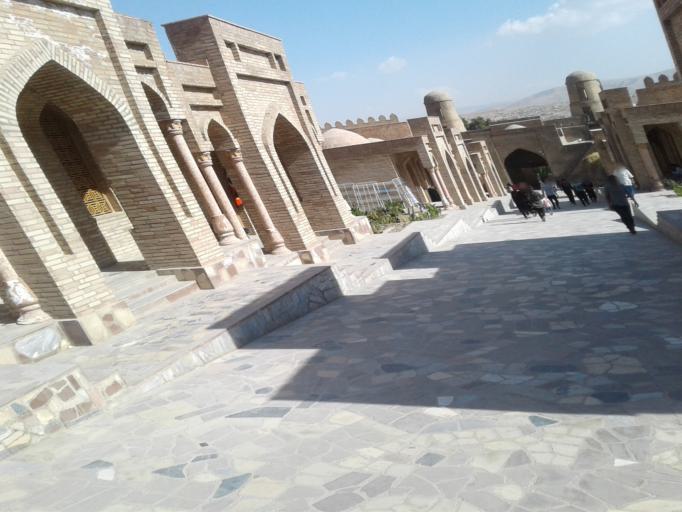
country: TJ
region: Republican Subordination
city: Hisor
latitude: 38.4841
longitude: 68.5928
